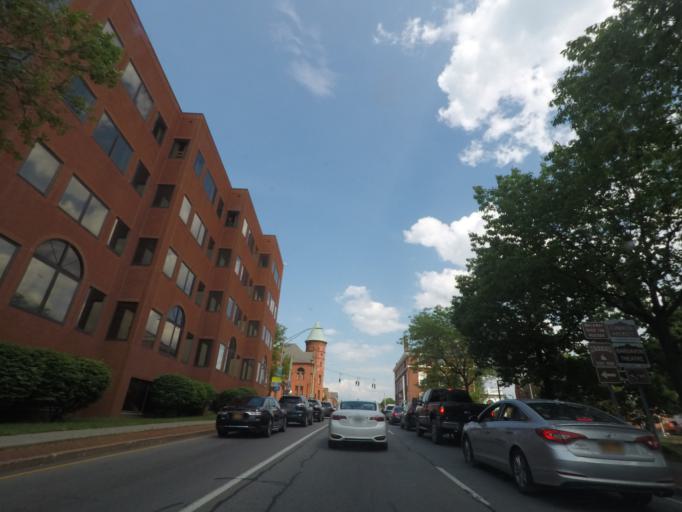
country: US
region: New York
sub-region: Dutchess County
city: Poughkeepsie
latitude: 41.7021
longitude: -73.9305
